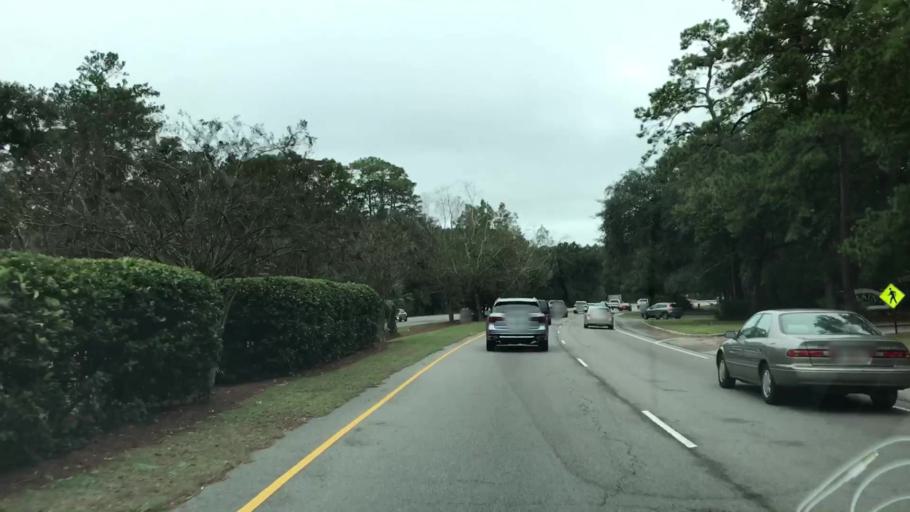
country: US
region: South Carolina
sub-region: Beaufort County
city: Hilton Head Island
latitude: 32.2135
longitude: -80.7231
